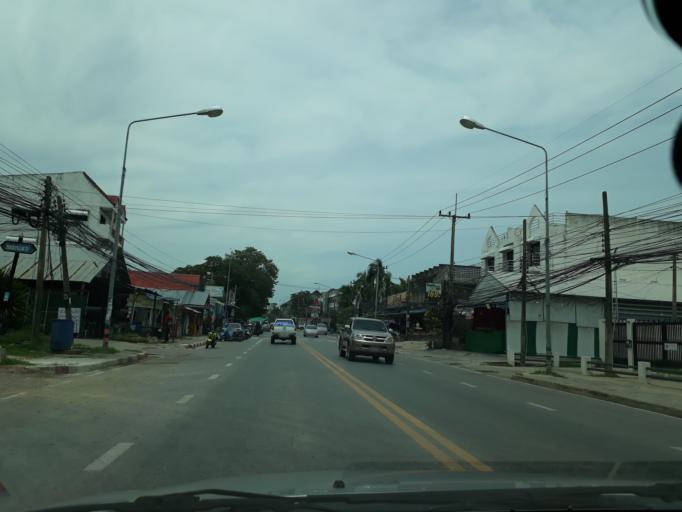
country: TH
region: Khon Kaen
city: Khon Kaen
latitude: 16.4349
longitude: 102.8560
